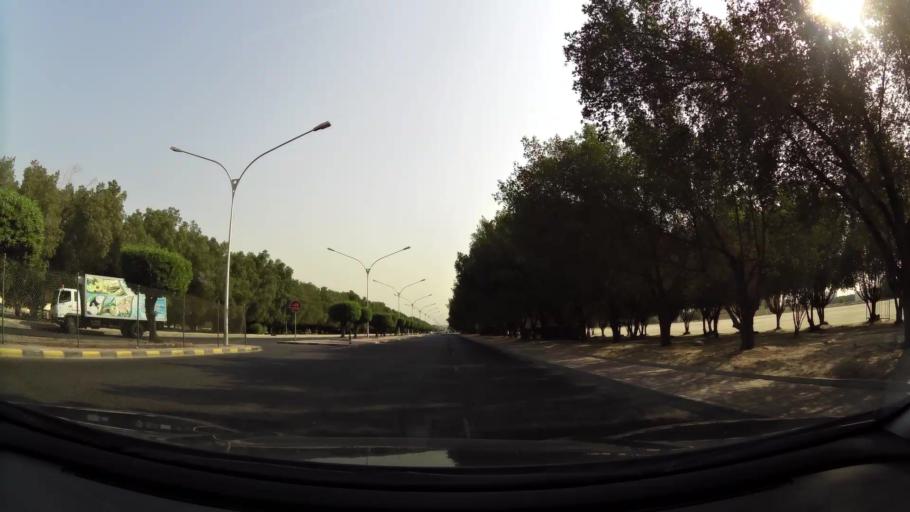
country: KW
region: Mubarak al Kabir
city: Sabah as Salim
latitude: 29.2770
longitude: 48.0633
